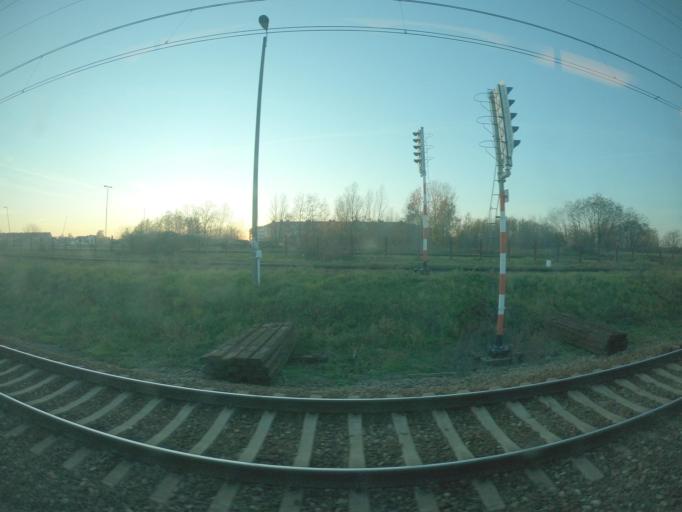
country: PL
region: Lubusz
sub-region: Powiat gorzowski
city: Kostrzyn nad Odra
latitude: 52.5968
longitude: 14.6487
